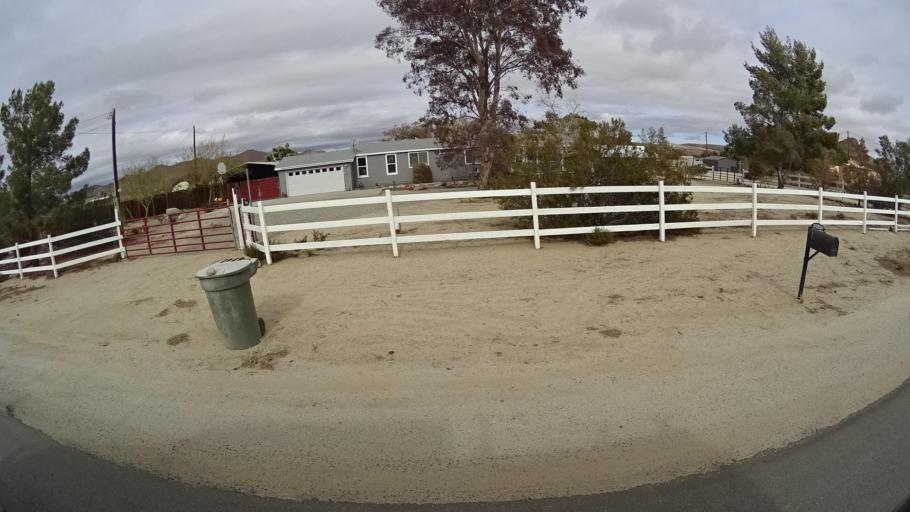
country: US
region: California
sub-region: Kern County
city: Rosamond
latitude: 34.8927
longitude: -118.2143
